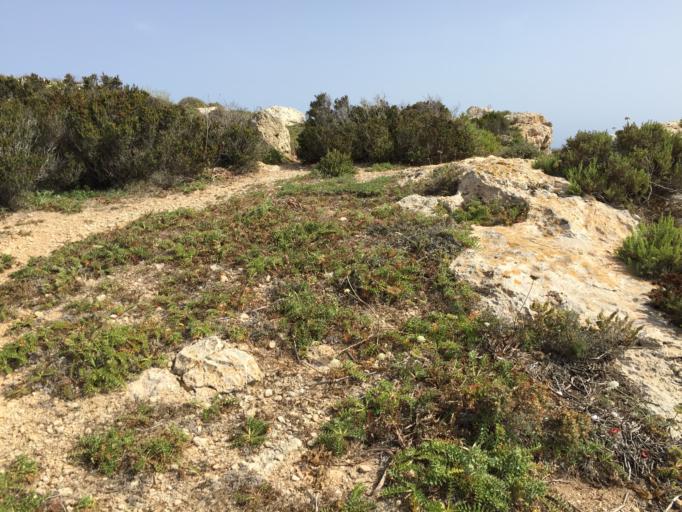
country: MT
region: Birzebbuga
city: Birzebbuga
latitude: 35.8079
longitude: 14.5104
